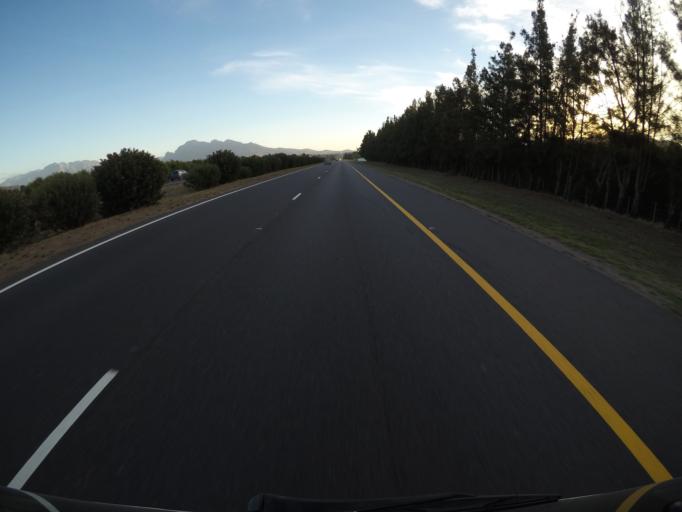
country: ZA
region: Western Cape
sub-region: Cape Winelands District Municipality
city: Paarl
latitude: -33.7509
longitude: 18.9918
